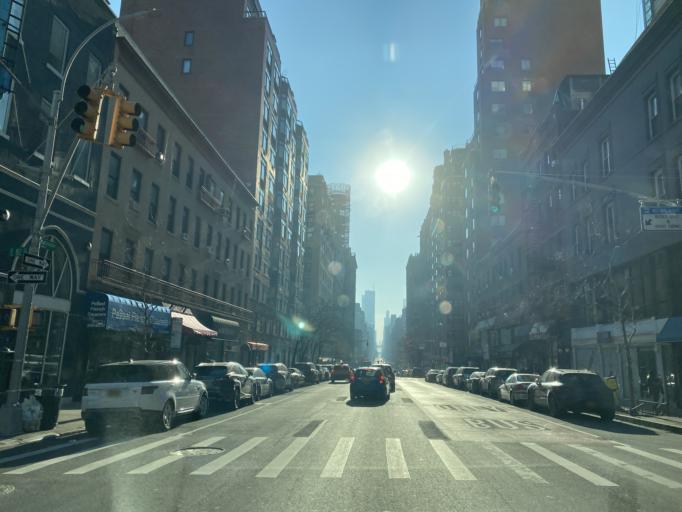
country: US
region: New York
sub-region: New York County
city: Manhattan
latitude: 40.7769
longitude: -73.9575
